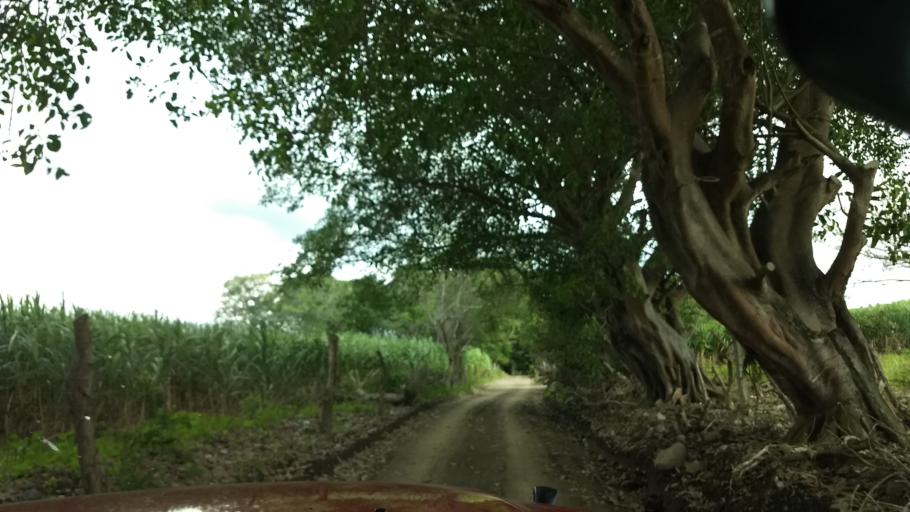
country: MX
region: Colima
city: Suchitlan
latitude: 19.4620
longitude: -103.7533
